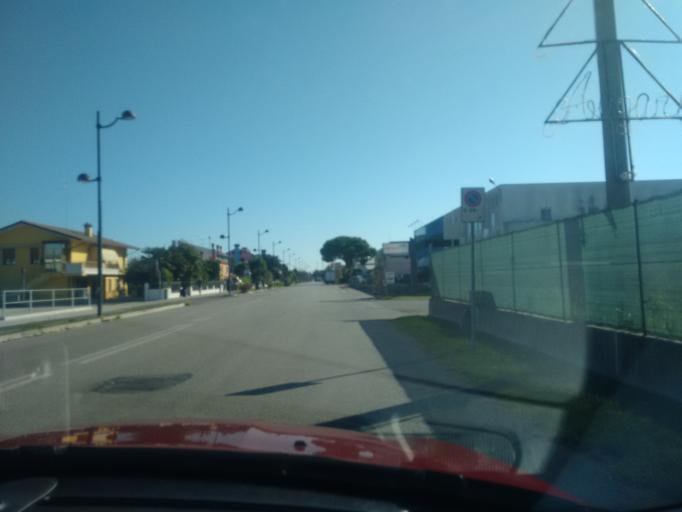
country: IT
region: Veneto
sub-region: Provincia di Venezia
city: Caorle
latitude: 45.6015
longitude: 12.8720
